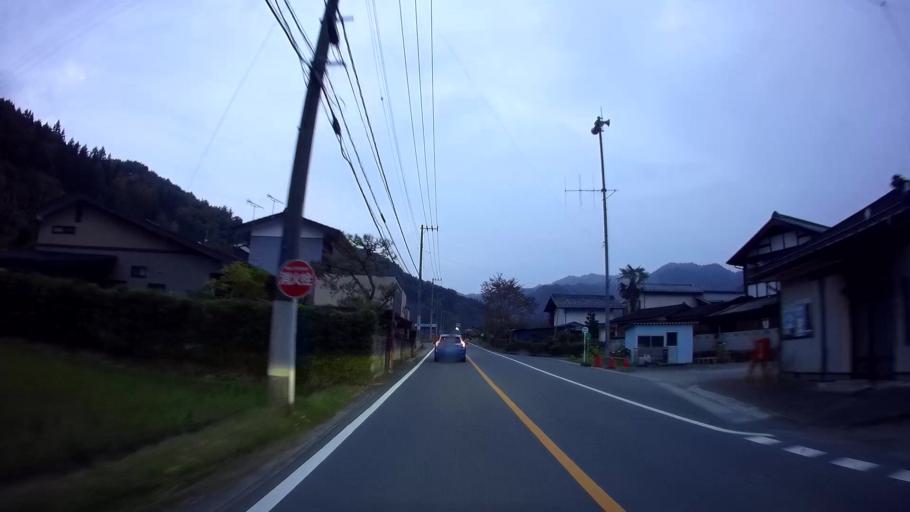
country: JP
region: Gunma
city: Nakanojomachi
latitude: 36.5358
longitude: 138.7856
